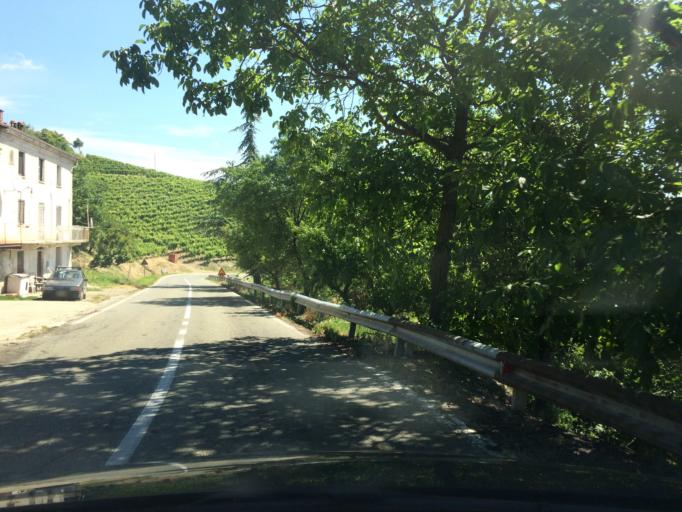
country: IT
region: Piedmont
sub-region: Provincia di Asti
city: Castel Rocchero
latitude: 44.7266
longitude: 8.4273
